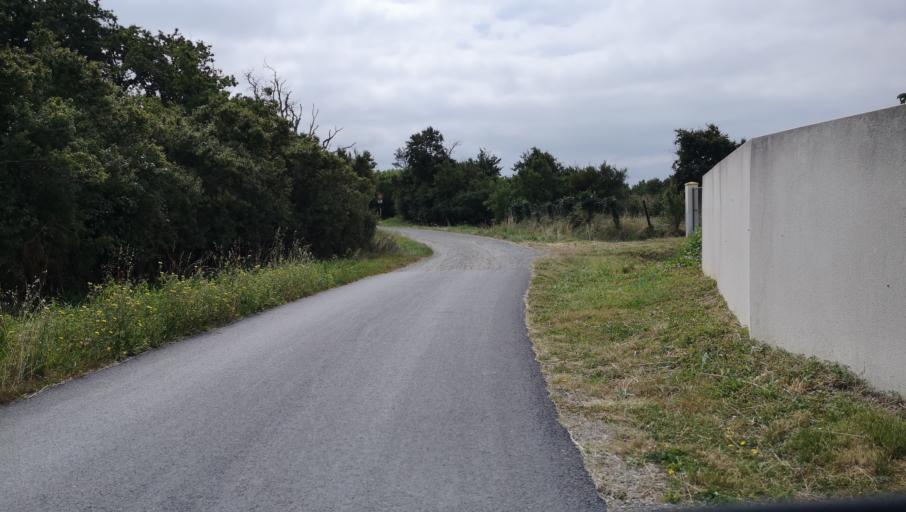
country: FR
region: Pays de la Loire
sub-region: Departement de la Vendee
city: Olonne-sur-Mer
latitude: 46.5703
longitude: -1.7882
